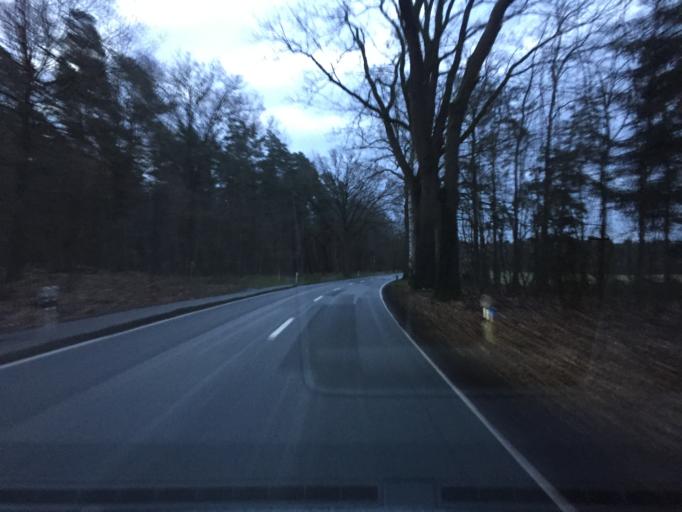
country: DE
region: Lower Saxony
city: Steyerberg
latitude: 52.5837
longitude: 8.9941
